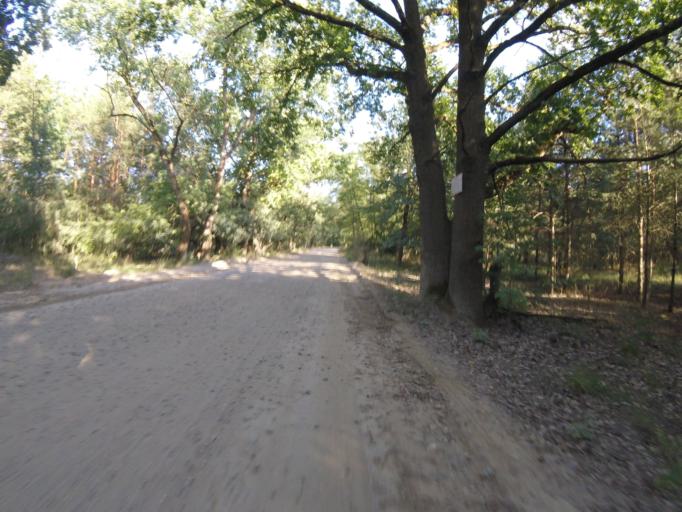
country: DE
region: Brandenburg
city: Zossen
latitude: 52.2017
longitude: 13.4990
